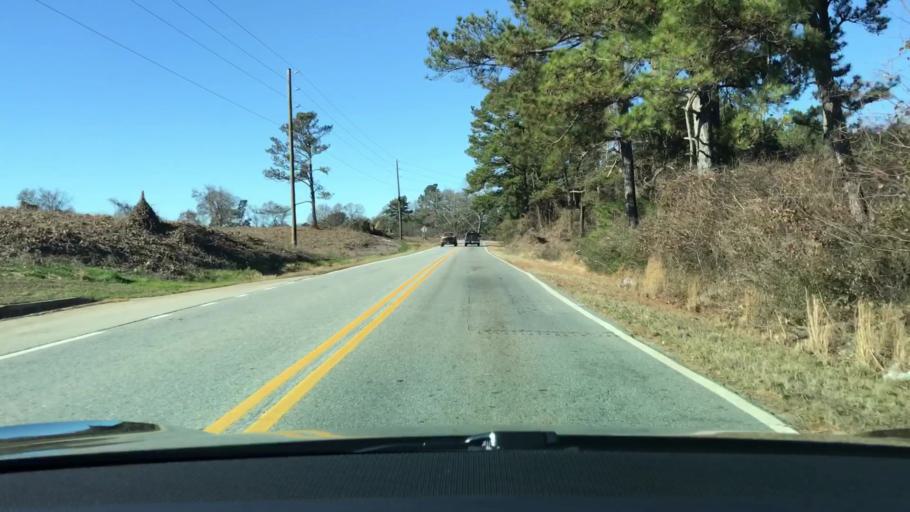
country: US
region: Georgia
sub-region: Barrow County
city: Winder
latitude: 33.9599
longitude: -83.7710
